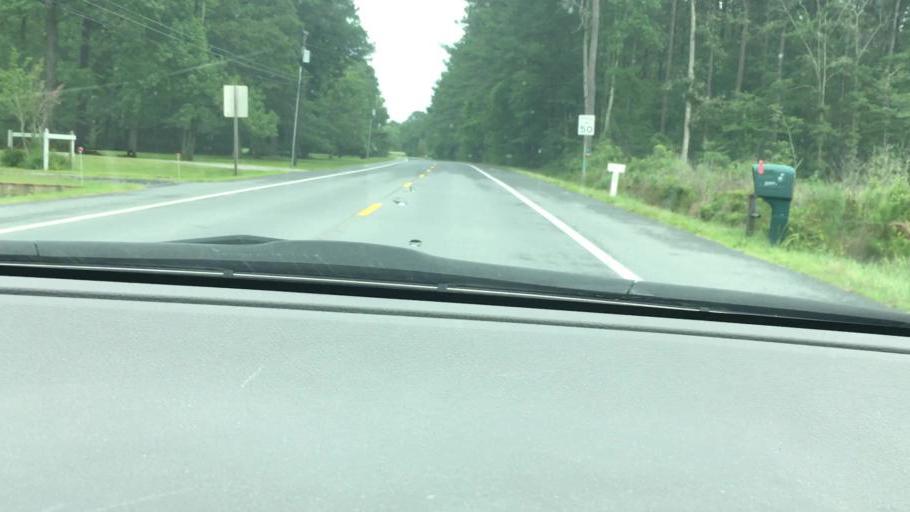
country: US
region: Maryland
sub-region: Worcester County
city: Pocomoke City
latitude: 38.0656
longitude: -75.5242
